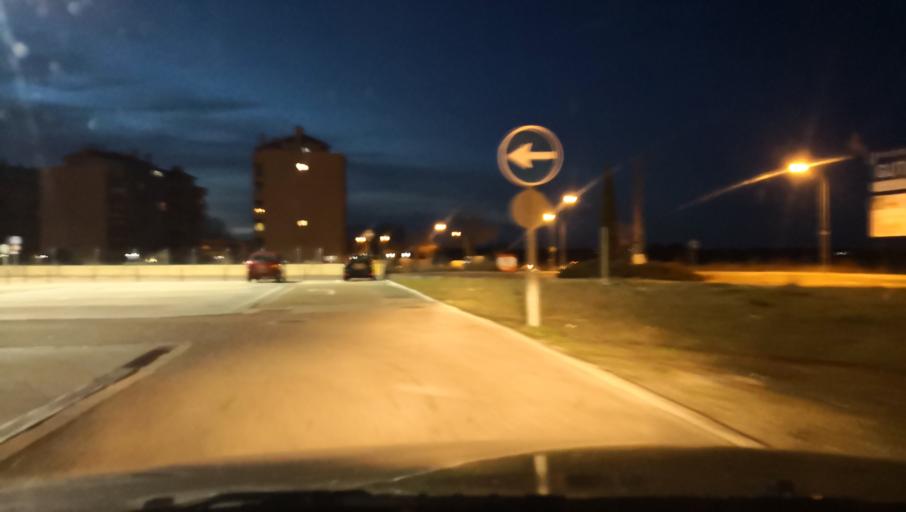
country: ES
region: Castille and Leon
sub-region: Provincia de Zamora
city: Zamora
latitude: 41.5216
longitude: -5.7210
